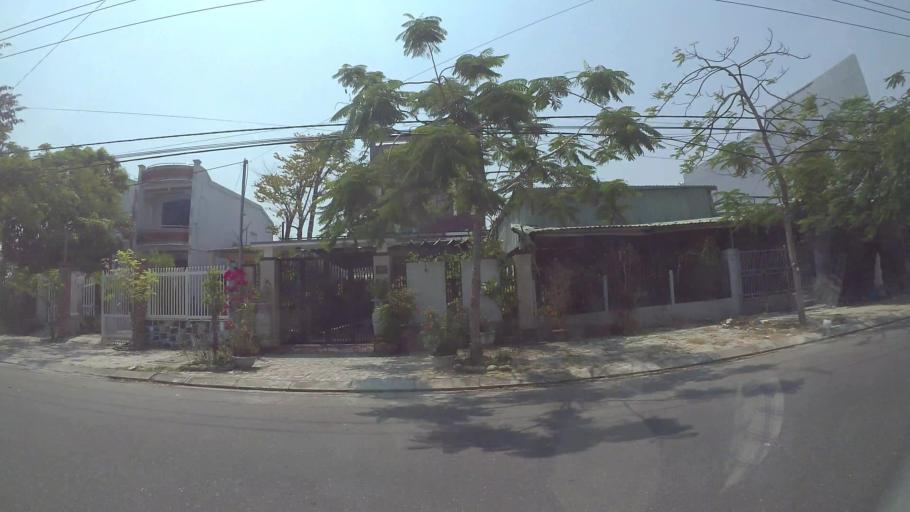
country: VN
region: Da Nang
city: Ngu Hanh Son
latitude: 15.9914
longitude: 108.2666
